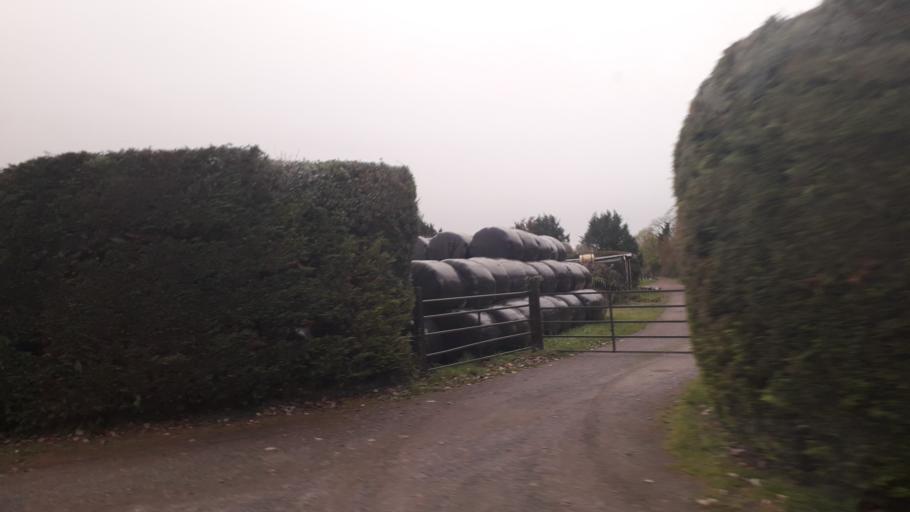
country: IE
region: Leinster
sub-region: Uibh Fhaili
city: Birr
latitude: 52.9900
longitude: -7.9244
